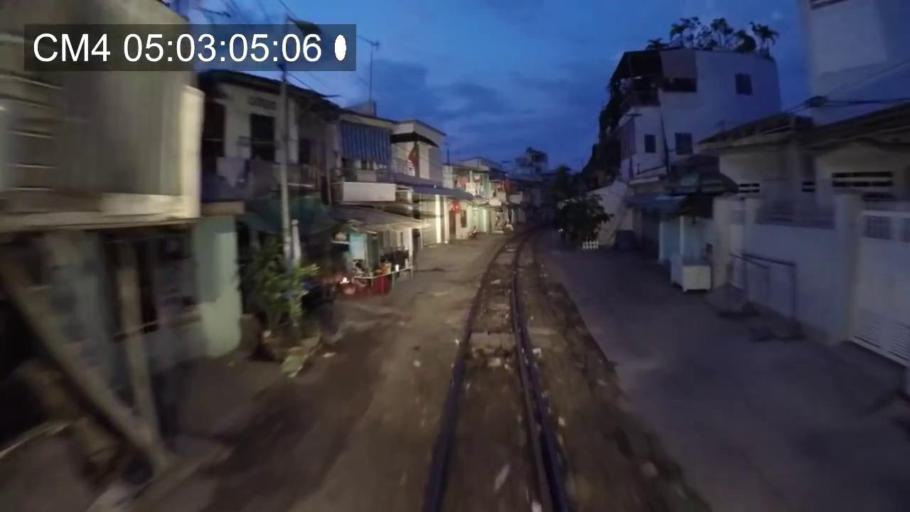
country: VN
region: Khanh Hoa
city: Nha Trang
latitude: 12.2532
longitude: 109.1714
